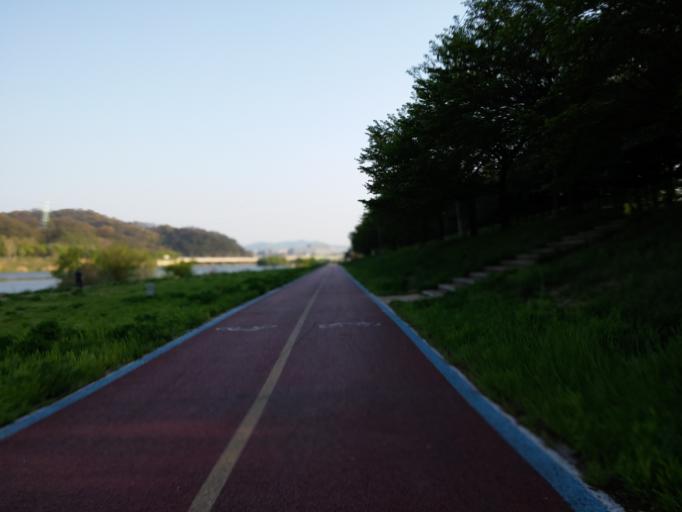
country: KR
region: Daejeon
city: Songgang-dong
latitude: 36.3894
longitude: 127.4099
